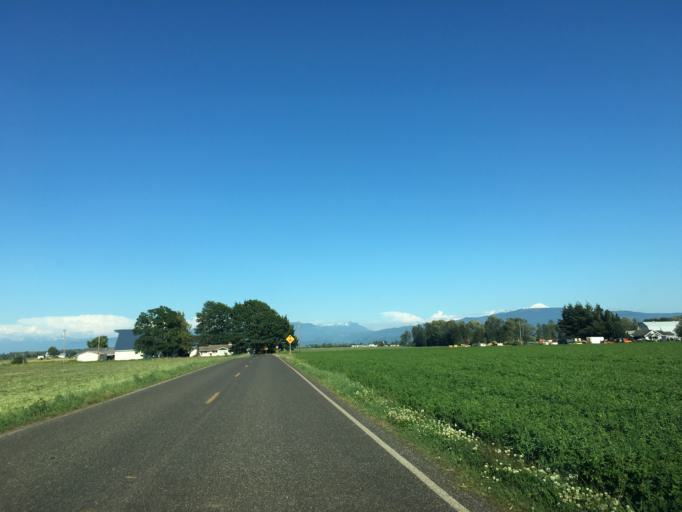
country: US
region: Washington
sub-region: Whatcom County
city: Lynden
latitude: 48.9865
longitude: -122.4549
